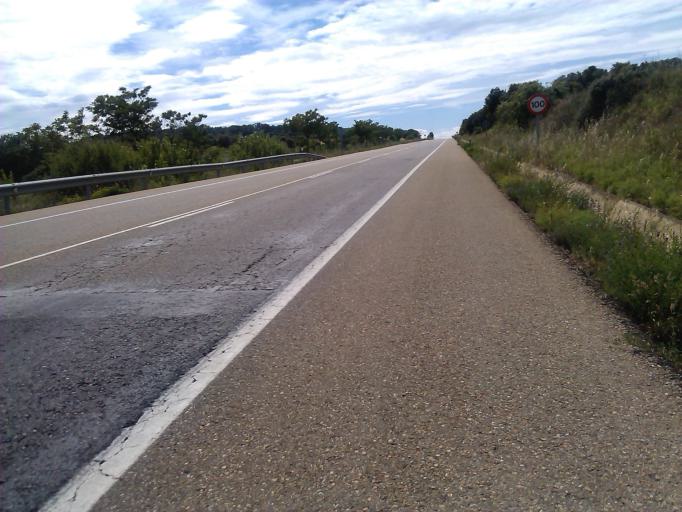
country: ES
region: Castille and Leon
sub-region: Provincia de Leon
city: Villarejo de Orbigo
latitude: 42.4466
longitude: -5.9474
